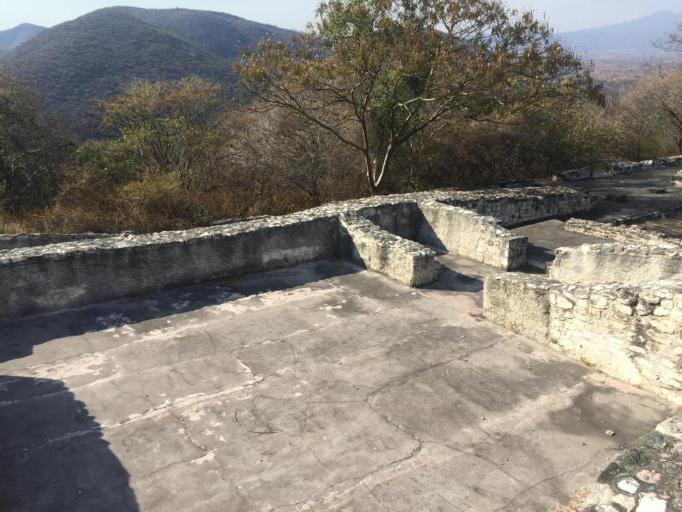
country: MX
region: Morelos
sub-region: Miacatlan
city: Xochicalco (Cirenio Longares)
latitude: 18.8046
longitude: -99.2977
